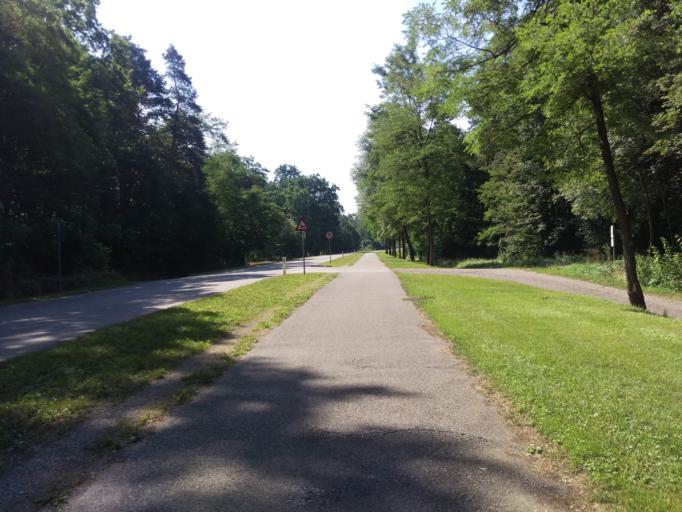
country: AT
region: Styria
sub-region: Politischer Bezirk Graz-Umgebung
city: Feldkirchen bei Graz
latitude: 47.0051
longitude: 15.4685
